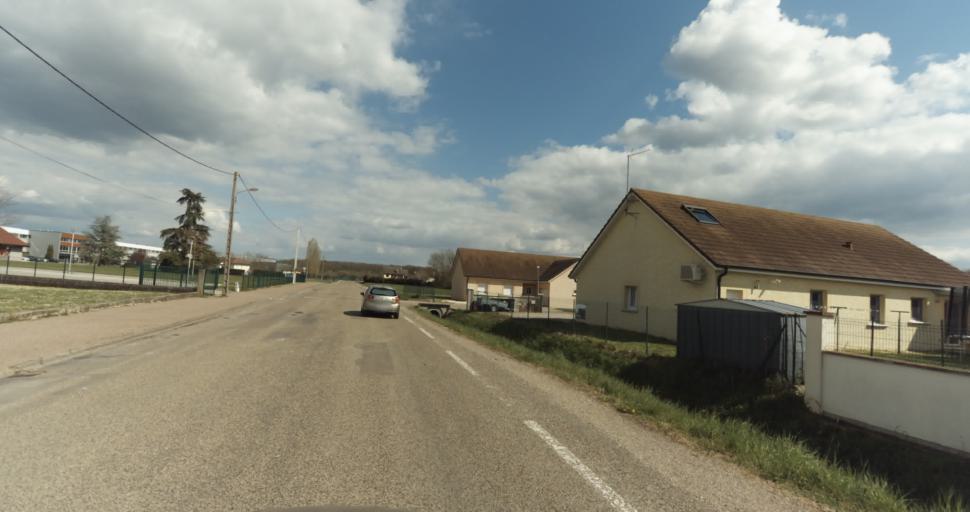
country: FR
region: Bourgogne
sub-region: Departement de la Cote-d'Or
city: Auxonne
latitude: 47.1911
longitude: 5.4101
